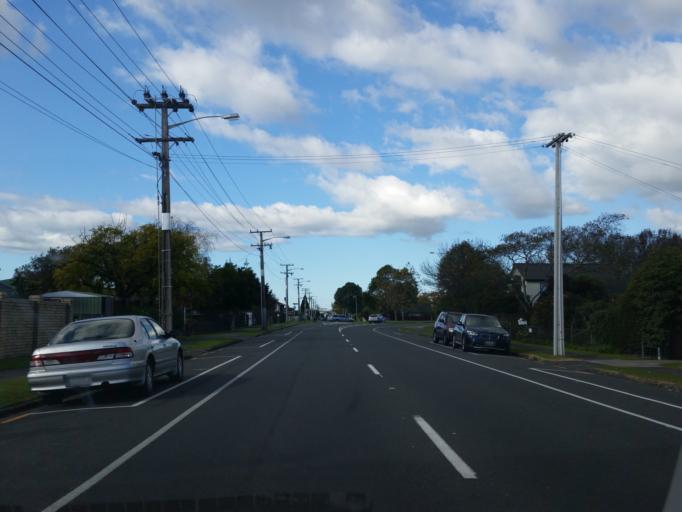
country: NZ
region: Bay of Plenty
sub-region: Tauranga City
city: Tauranga
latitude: -37.6680
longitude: 176.1548
